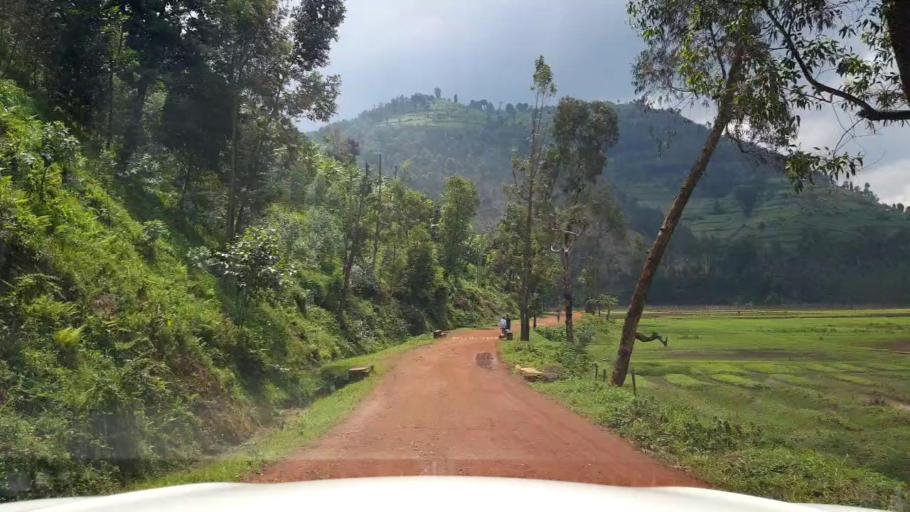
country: UG
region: Western Region
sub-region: Kisoro District
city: Kisoro
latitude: -1.3820
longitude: 29.7962
